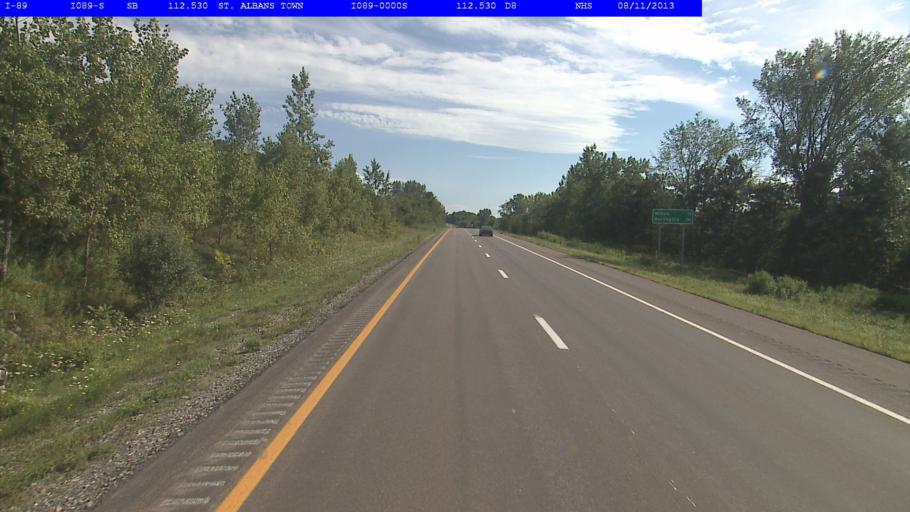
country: US
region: Vermont
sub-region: Franklin County
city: Saint Albans
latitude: 44.7777
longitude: -73.0744
